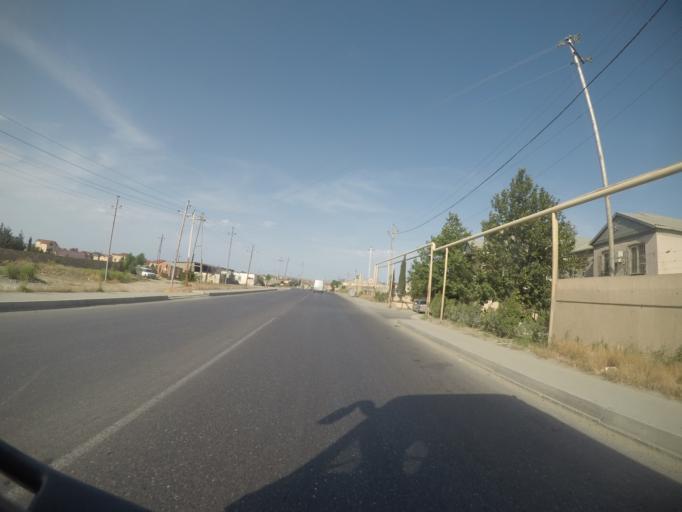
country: AZ
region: Baki
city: Bilajari
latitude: 40.4442
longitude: 49.7911
